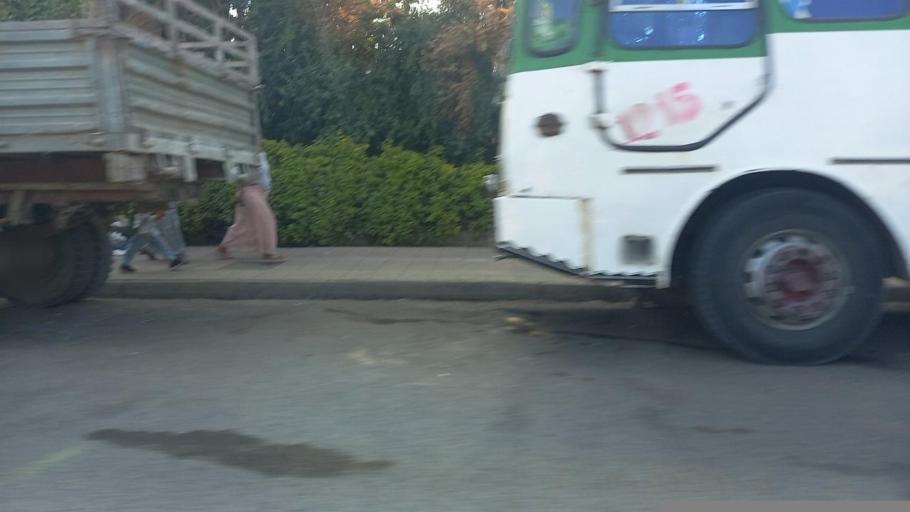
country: ET
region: Adis Abeba
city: Addis Ababa
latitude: 8.9394
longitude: 38.7485
